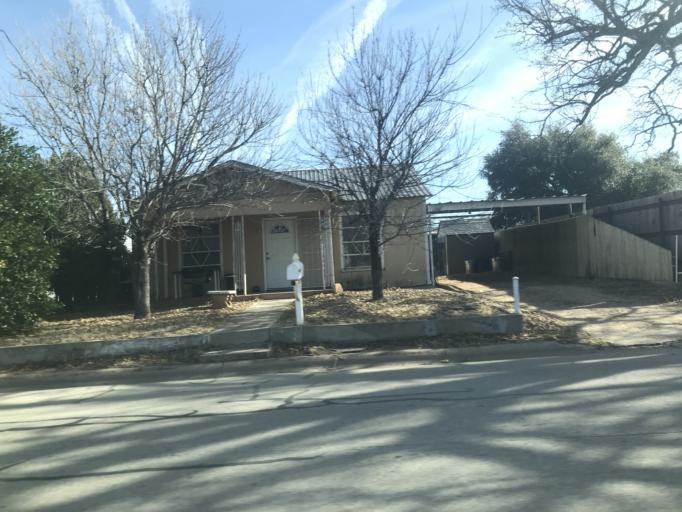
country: US
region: Texas
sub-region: Taylor County
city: Abilene
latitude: 32.4862
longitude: -99.7393
